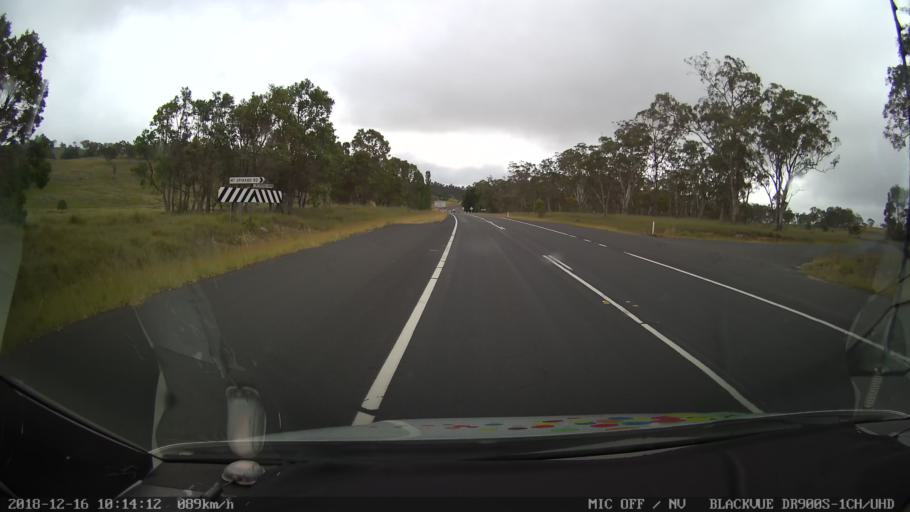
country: AU
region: New South Wales
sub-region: Tenterfield Municipality
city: Carrolls Creek
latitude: -29.2896
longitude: 151.9610
